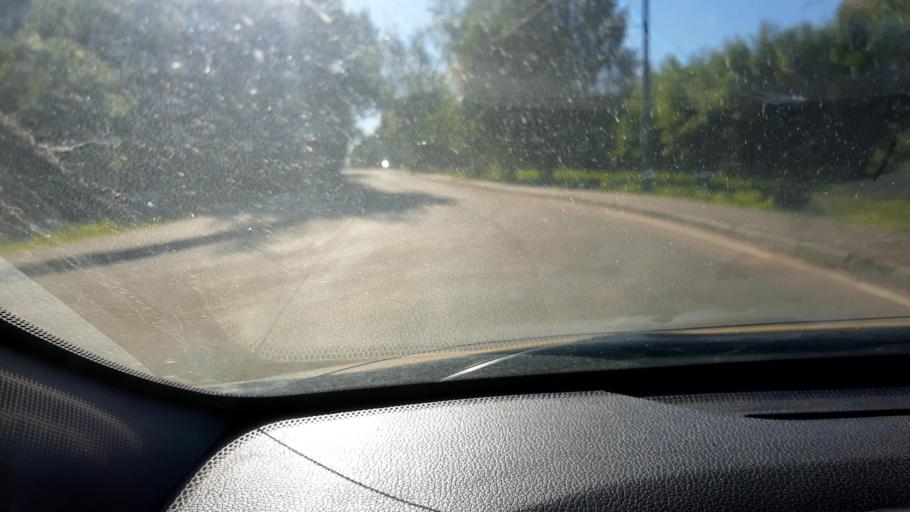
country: RU
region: Moskovskaya
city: Vatutinki
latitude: 55.5025
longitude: 37.3211
